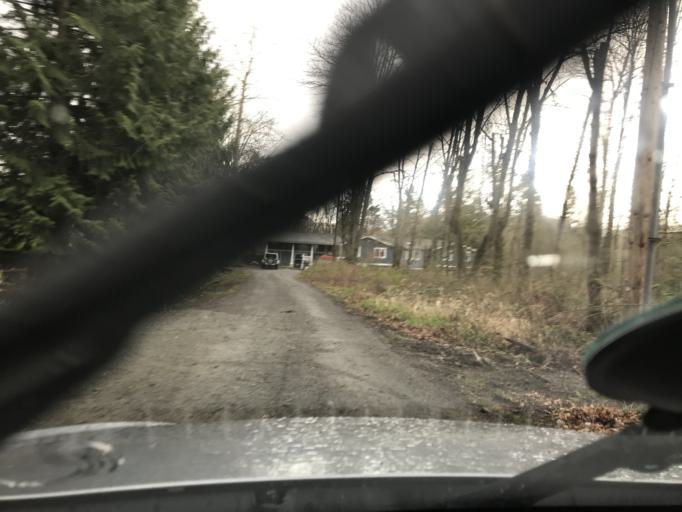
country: US
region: Washington
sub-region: King County
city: Ames Lake
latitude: 47.6464
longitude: -122.0003
